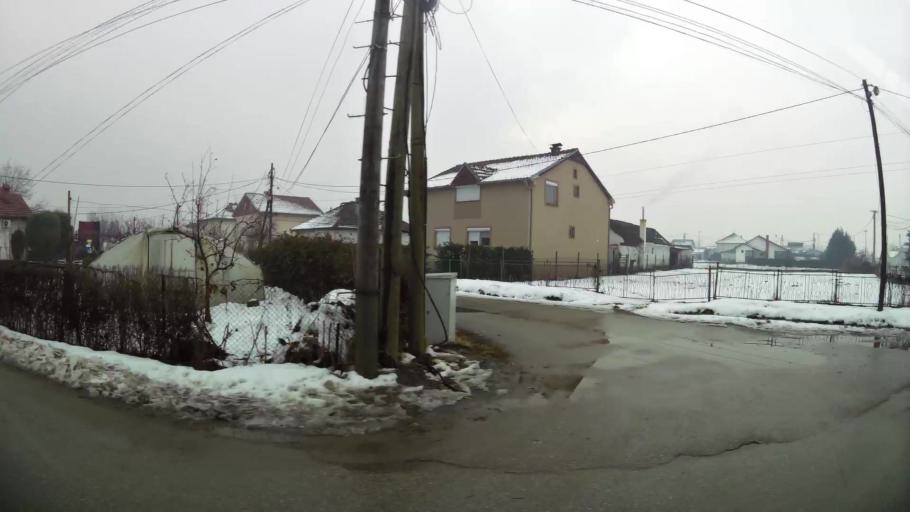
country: MK
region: Petrovec
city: Petrovec
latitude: 41.9370
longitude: 21.6105
